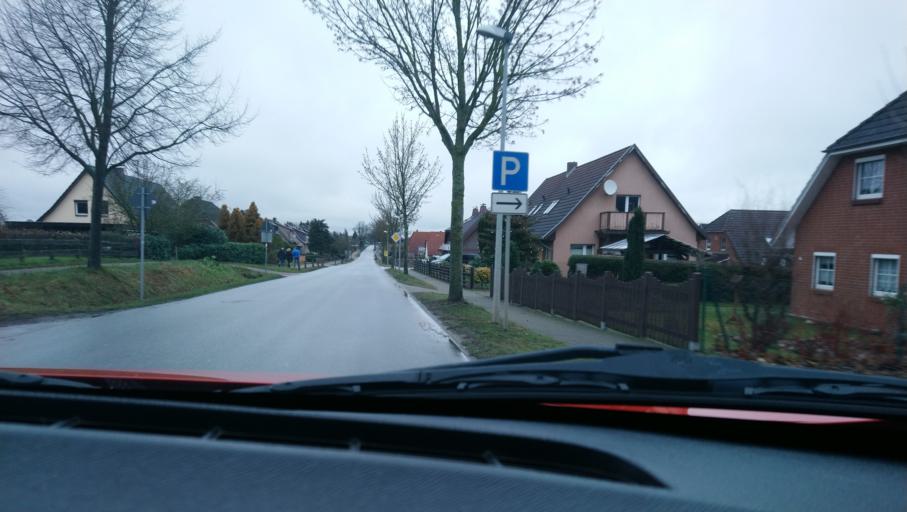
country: DE
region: Mecklenburg-Vorpommern
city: Seehof
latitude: 53.6908
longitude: 11.4309
